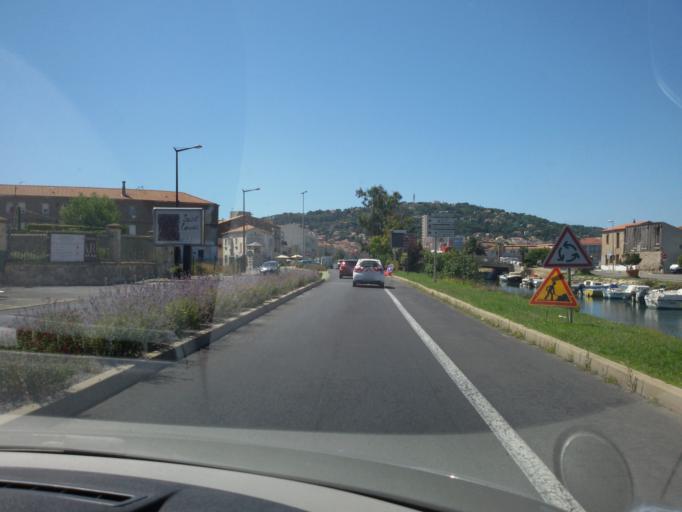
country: FR
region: Languedoc-Roussillon
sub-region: Departement de l'Herault
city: Sete
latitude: 43.4098
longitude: 3.7063
